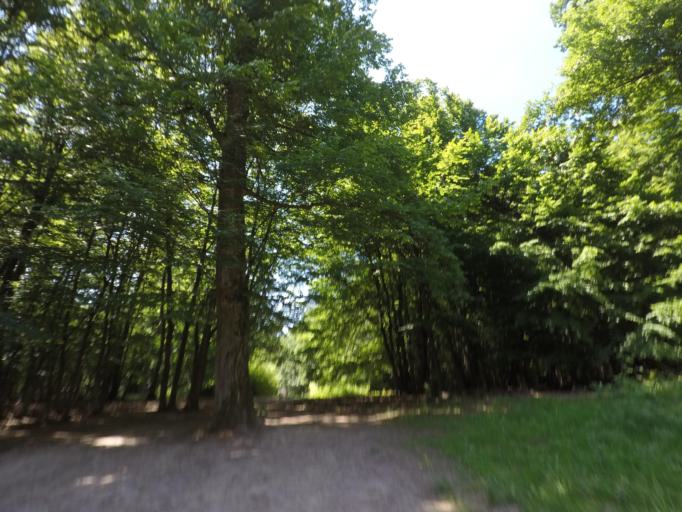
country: AT
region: Lower Austria
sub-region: Politischer Bezirk Modling
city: Perchtoldsdorf
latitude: 48.1797
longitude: 16.2468
